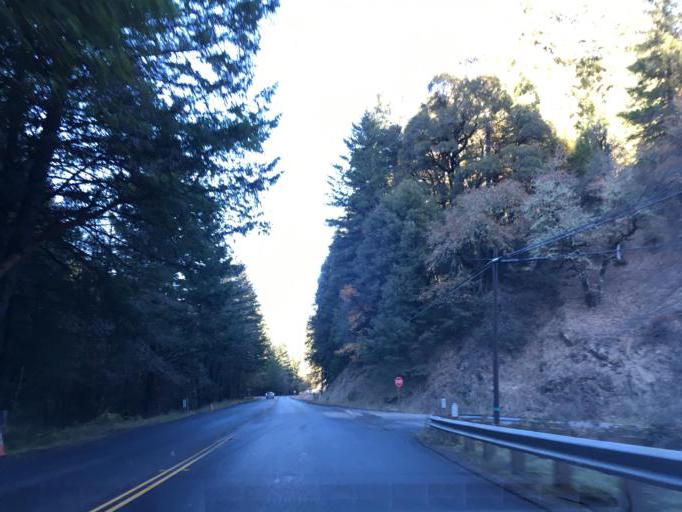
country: US
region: California
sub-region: Mendocino County
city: Laytonville
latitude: 39.7974
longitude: -123.5423
